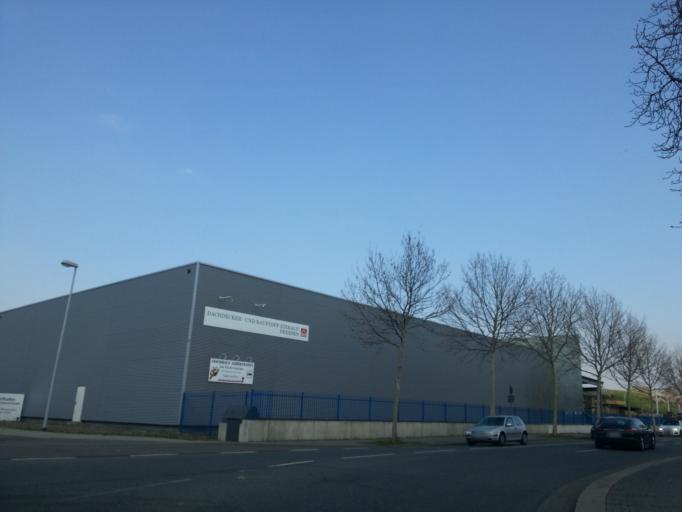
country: DE
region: Saxony
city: Dresden
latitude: 51.0628
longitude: 13.7135
